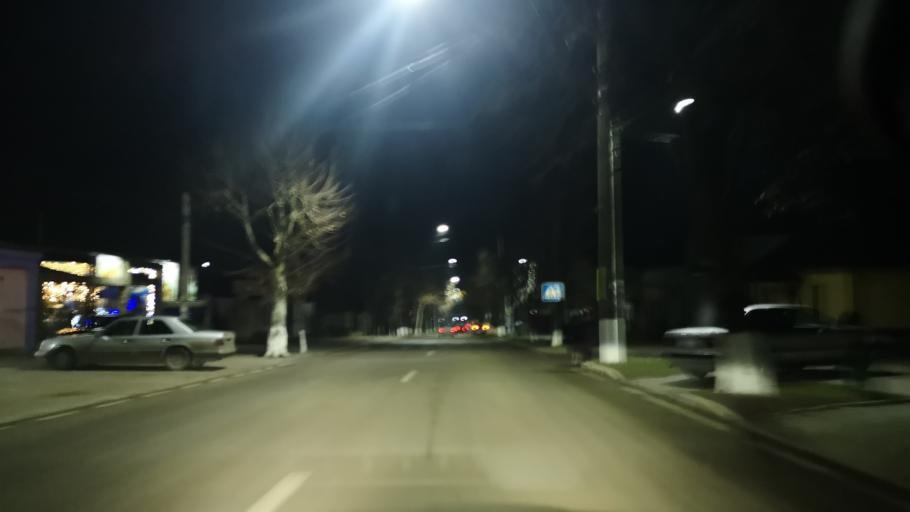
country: MD
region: Orhei
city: Orhei
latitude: 47.3840
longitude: 28.8254
